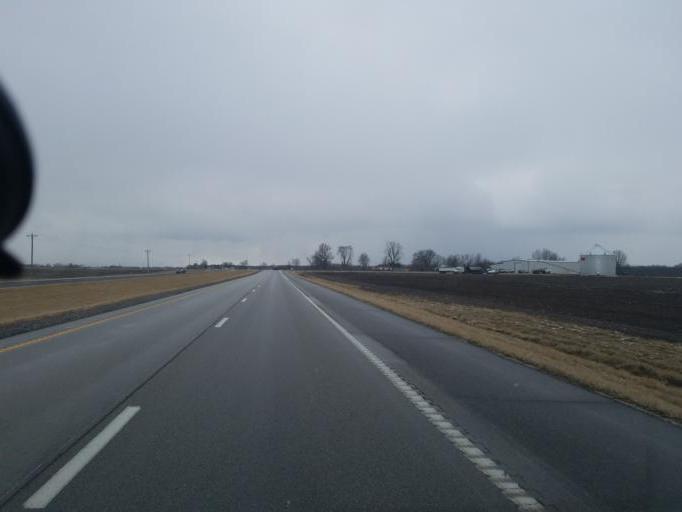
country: US
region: Missouri
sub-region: Macon County
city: Macon
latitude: 39.8501
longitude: -92.4801
